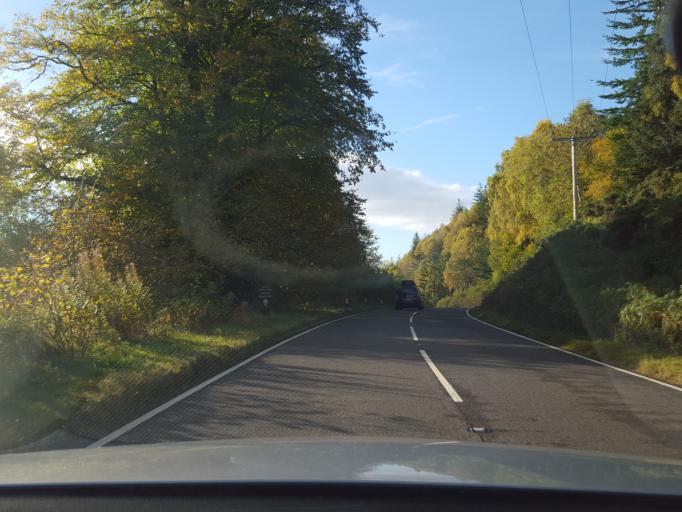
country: GB
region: Scotland
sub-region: Highland
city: Beauly
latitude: 57.2221
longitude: -4.5776
